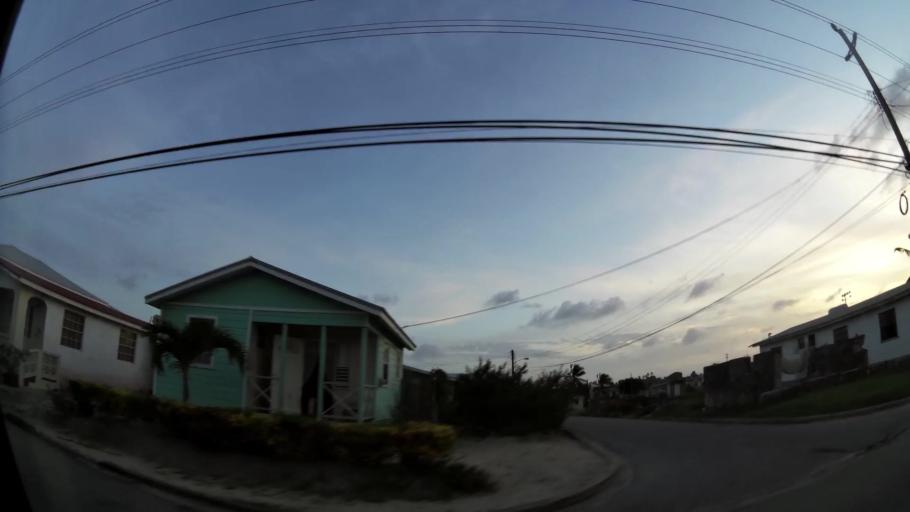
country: BB
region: Saint Philip
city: Crane
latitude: 13.1040
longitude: -59.4542
